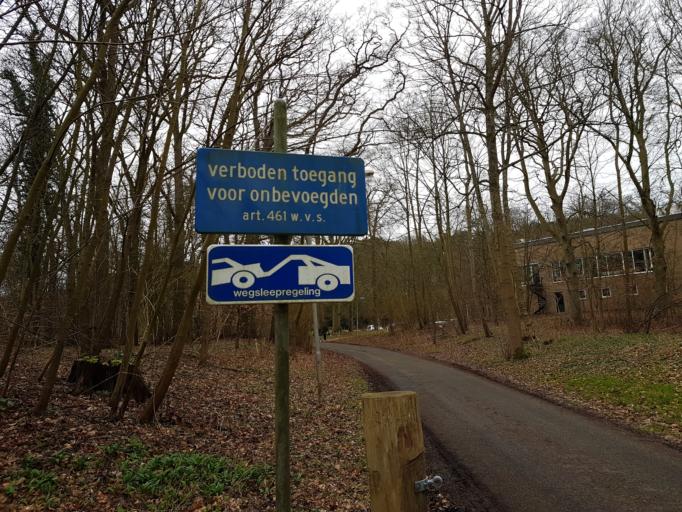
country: NL
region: North Holland
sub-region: Gemeente Bloemendaal
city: Bloemendaal
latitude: 52.3860
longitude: 4.5972
